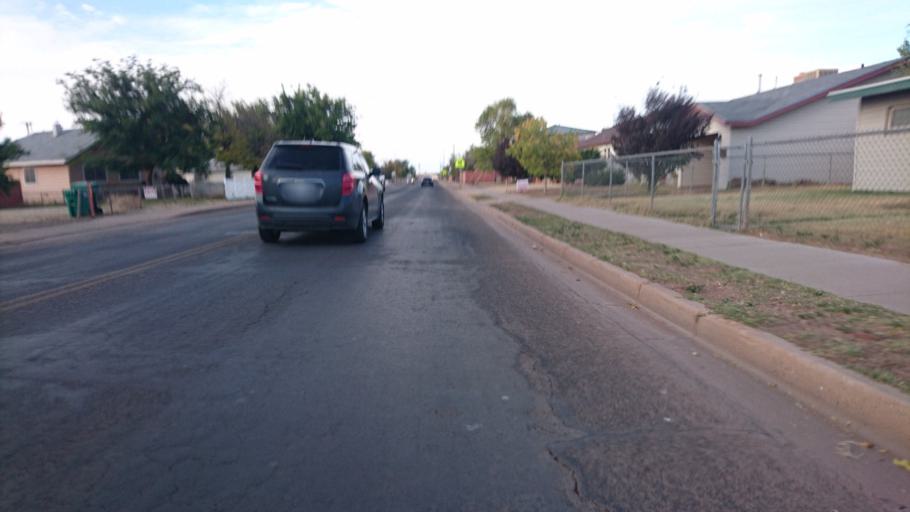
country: US
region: Arizona
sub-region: Navajo County
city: Winslow
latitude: 35.0313
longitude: -110.6977
